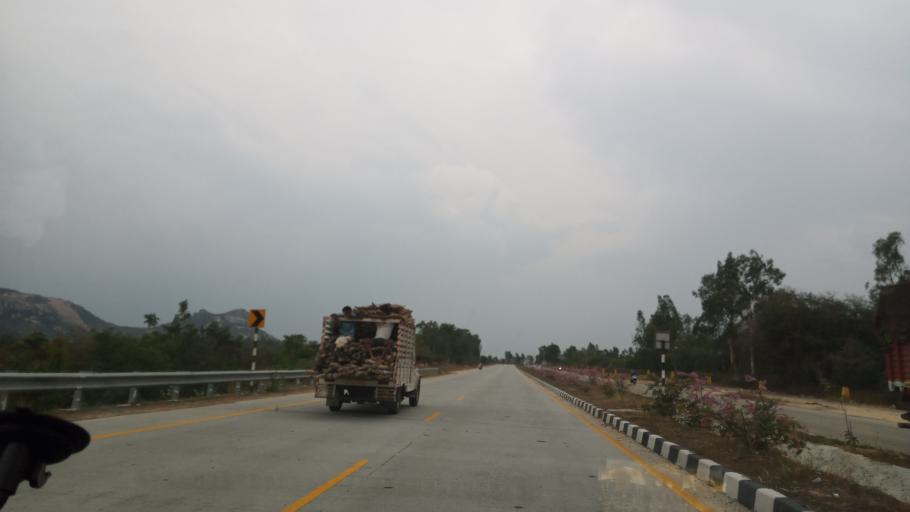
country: IN
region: Andhra Pradesh
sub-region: Chittoor
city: Palmaner
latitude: 13.1886
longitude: 78.6602
